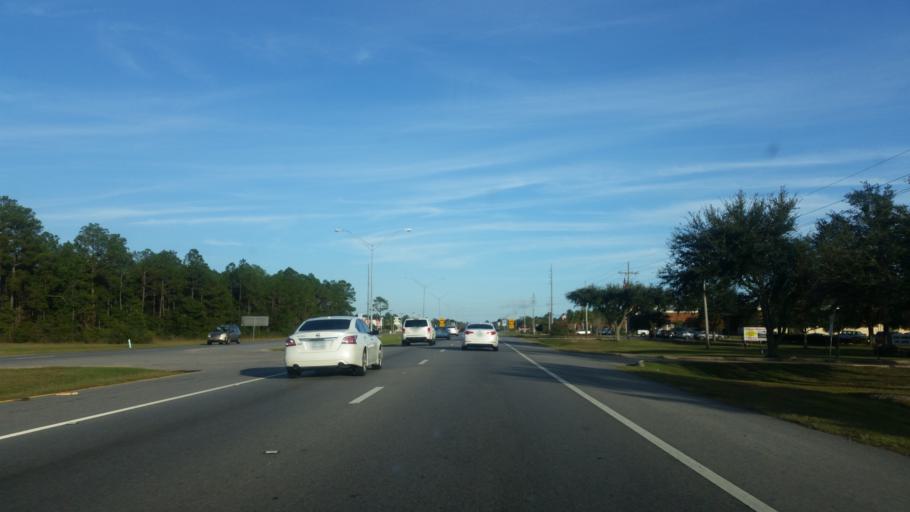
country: US
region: Mississippi
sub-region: Jackson County
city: Gulf Park Estates
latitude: 30.4101
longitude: -88.7671
